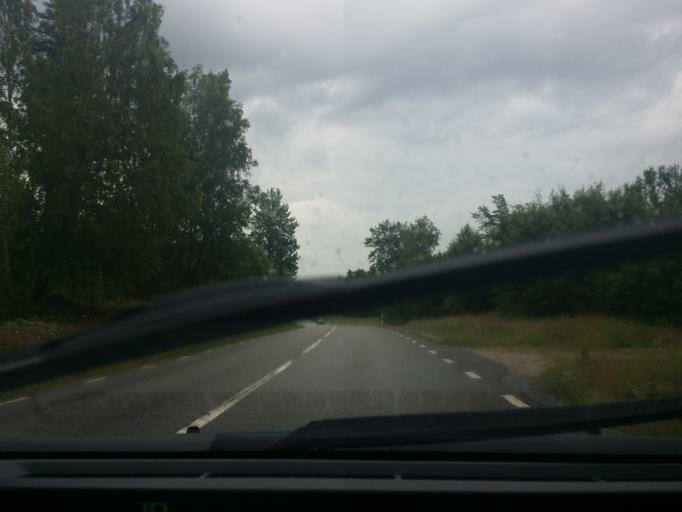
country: SE
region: OErebro
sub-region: Lindesbergs Kommun
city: Frovi
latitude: 59.4423
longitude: 15.2803
